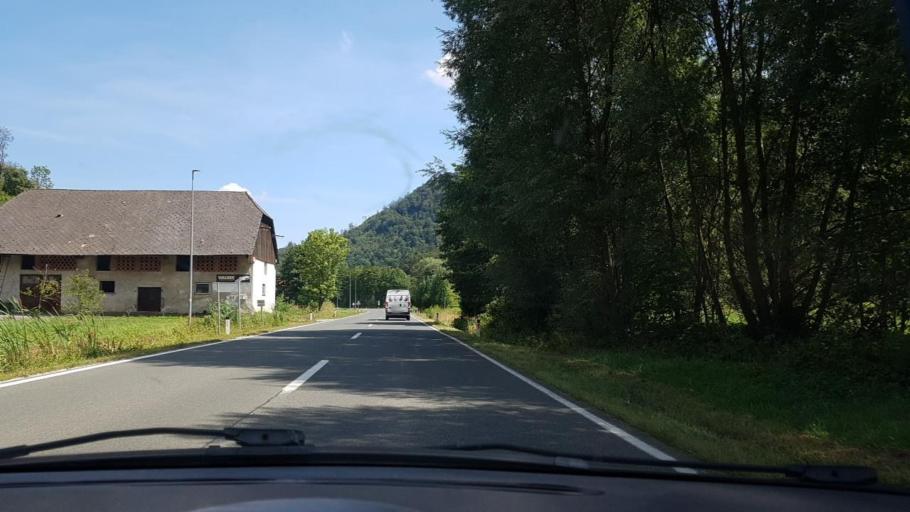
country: SI
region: Moravce
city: Moravce
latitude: 46.1655
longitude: 14.7566
